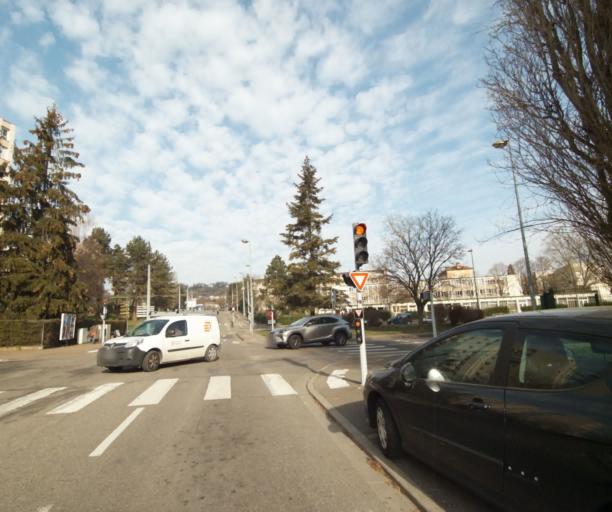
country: FR
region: Lorraine
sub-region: Departement de Meurthe-et-Moselle
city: Laxou
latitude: 48.6799
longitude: 6.1541
